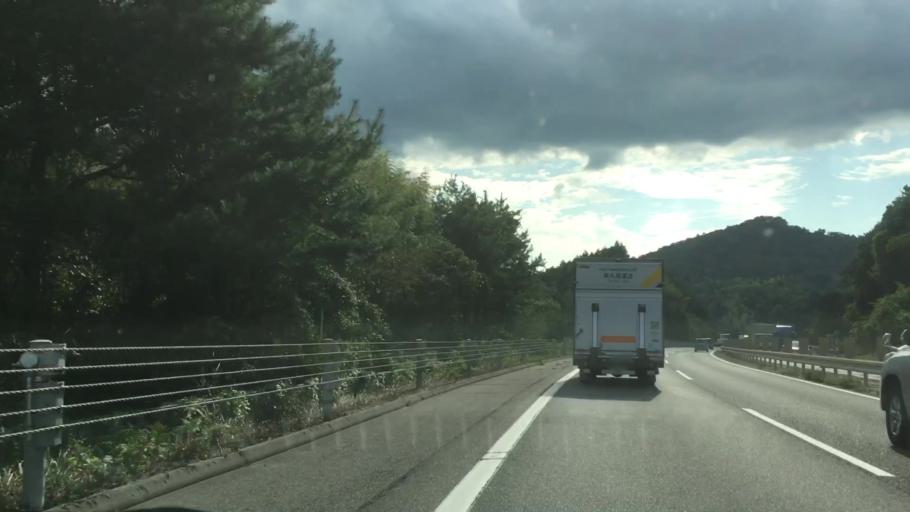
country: JP
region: Yamaguchi
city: Iwakuni
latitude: 34.1426
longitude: 132.1230
